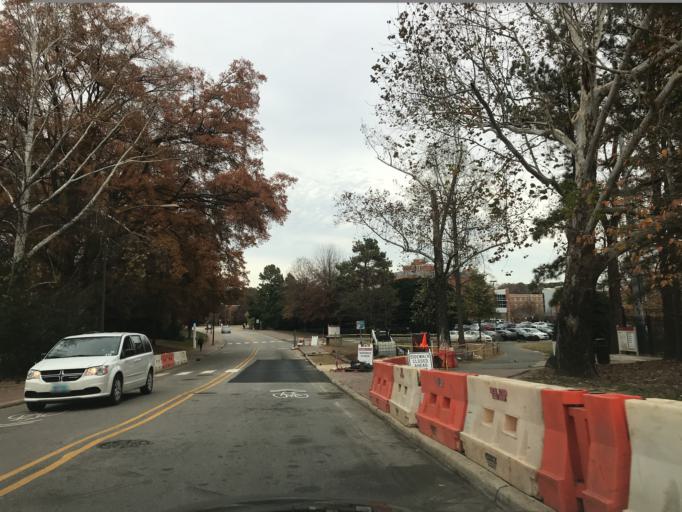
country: US
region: North Carolina
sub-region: Wake County
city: West Raleigh
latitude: 35.7838
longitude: -78.6770
